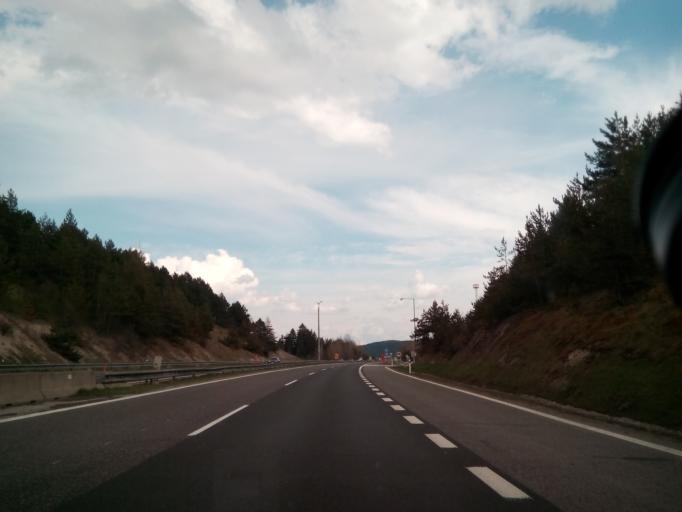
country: SK
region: Zilinsky
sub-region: Okres Zilina
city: Liptovsky Hradok
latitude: 49.0568
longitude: 19.6994
